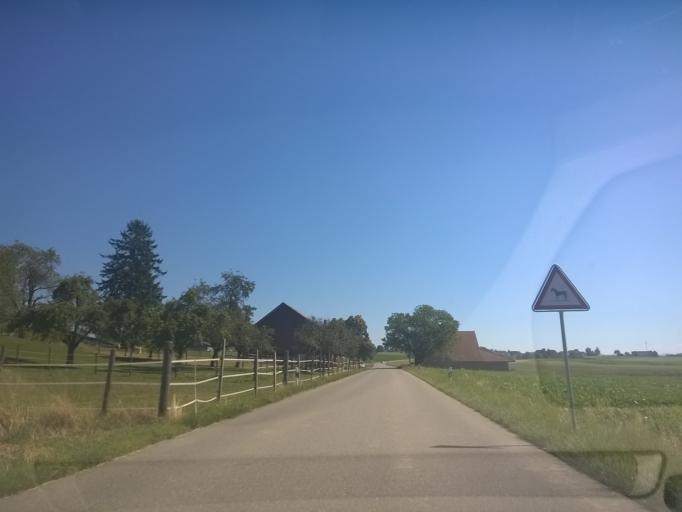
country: CH
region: Zurich
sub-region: Bezirk Winterthur
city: Brutten
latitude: 47.4716
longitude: 8.6547
